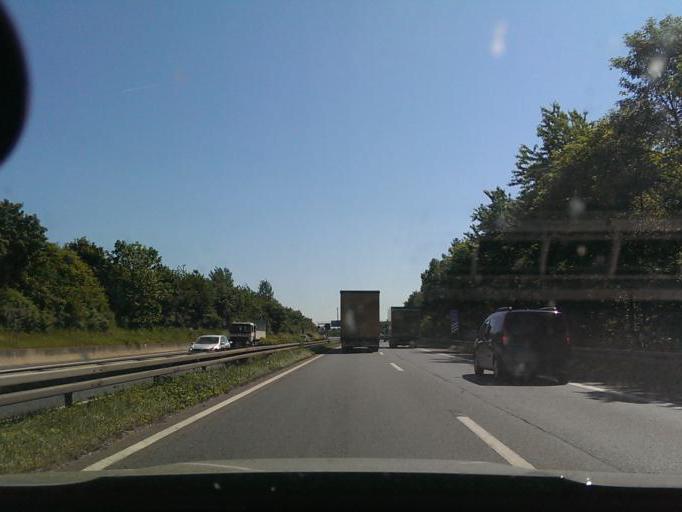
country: DE
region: Lower Saxony
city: Isernhagen Farster Bauerschaft
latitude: 52.4094
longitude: 9.8316
